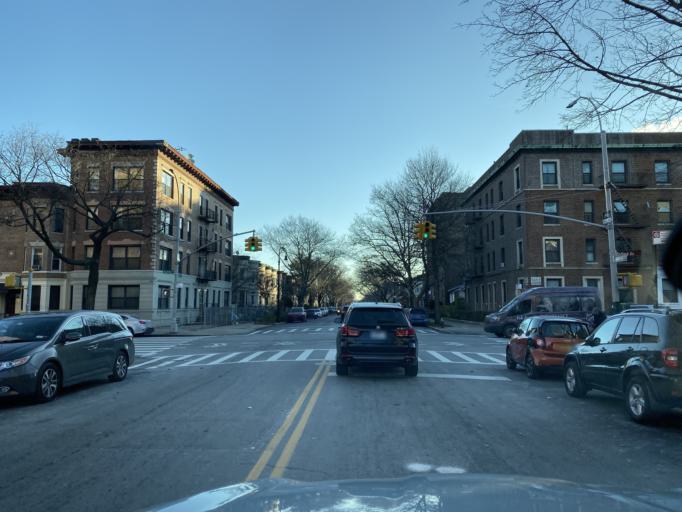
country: US
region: New York
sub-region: Kings County
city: Brooklyn
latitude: 40.6619
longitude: -73.9574
